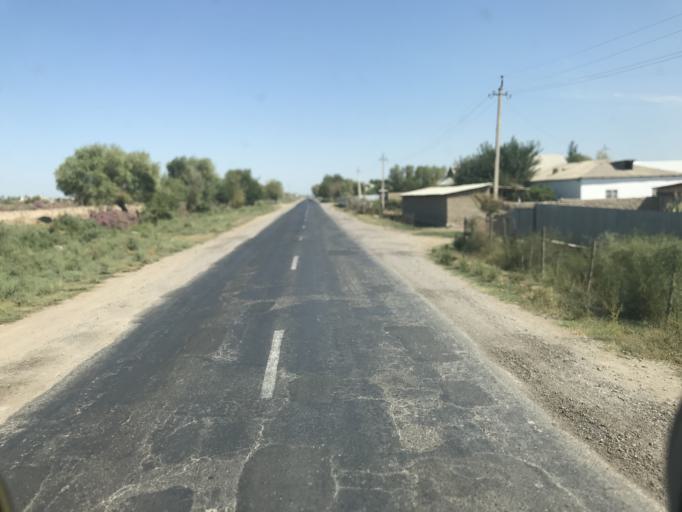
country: KZ
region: Ongtustik Qazaqstan
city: Ilyich
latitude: 40.7651
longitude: 68.5372
